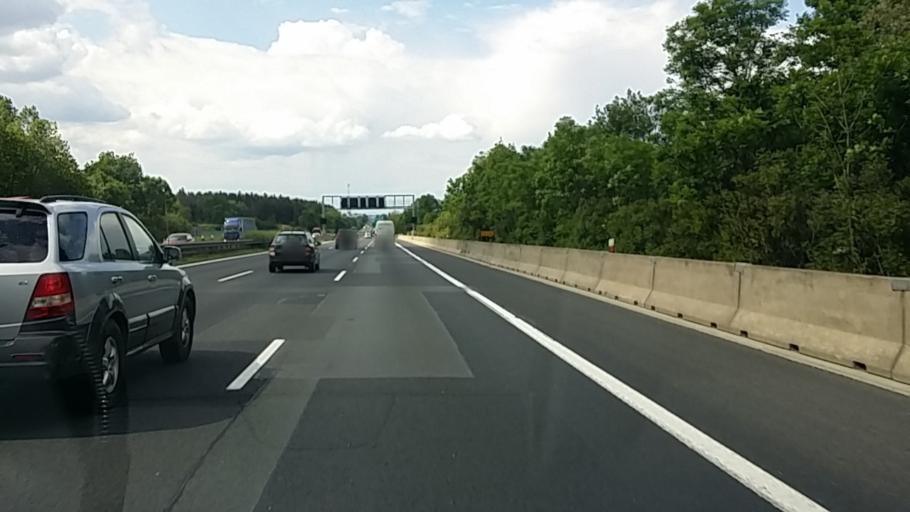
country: CZ
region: Central Bohemia
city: Velke Popovice
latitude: 49.9545
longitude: 14.6383
